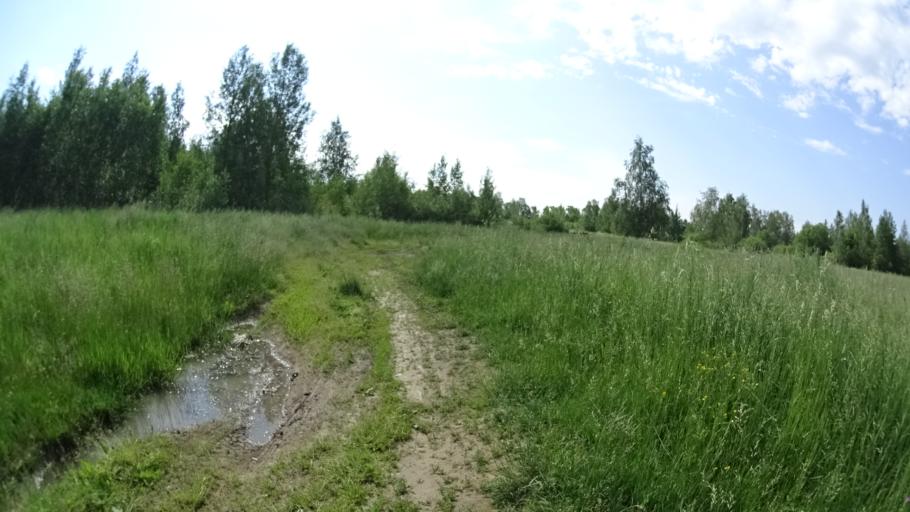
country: RU
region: Moskovskaya
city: Lesnoy
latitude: 56.0823
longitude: 37.9379
